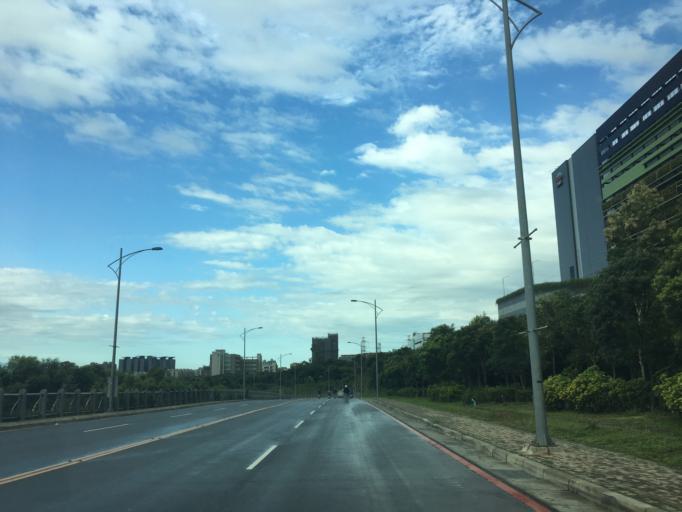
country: TW
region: Taiwan
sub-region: Taichung City
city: Taichung
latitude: 24.2090
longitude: 120.6107
